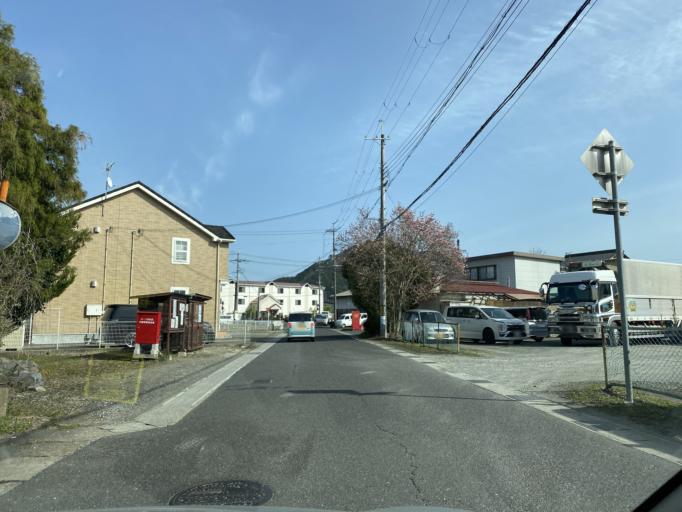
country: JP
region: Kyoto
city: Ayabe
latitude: 35.3050
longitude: 135.2307
